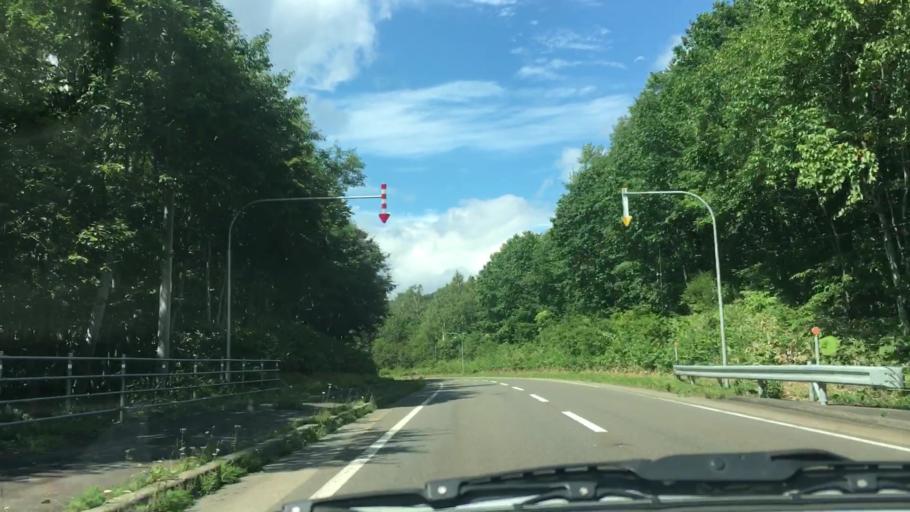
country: JP
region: Hokkaido
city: Otofuke
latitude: 43.3381
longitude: 143.2868
